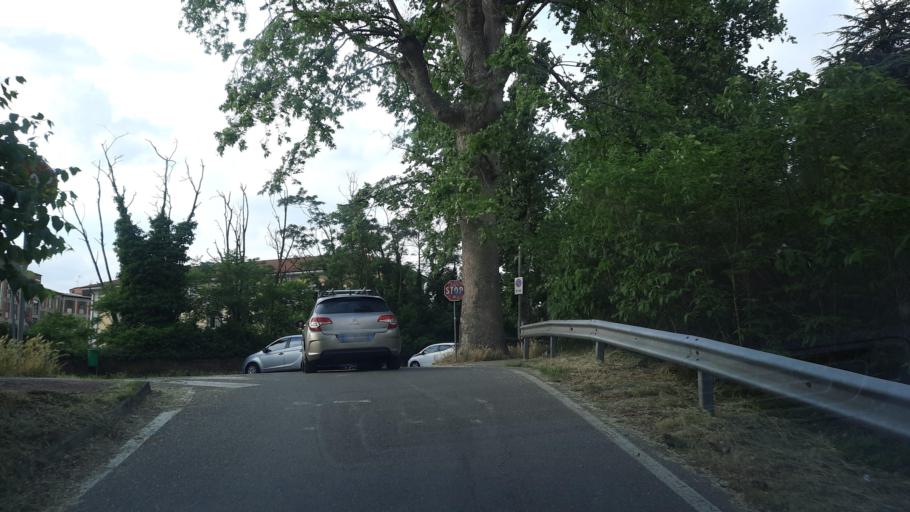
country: IT
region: Lombardy
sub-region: Provincia di Pavia
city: Pavia
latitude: 45.1925
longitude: 9.1523
